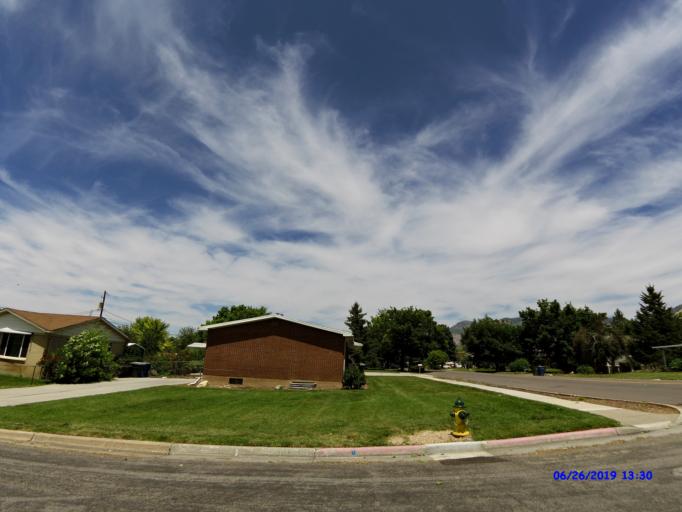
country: US
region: Utah
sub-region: Weber County
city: South Ogden
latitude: 41.2008
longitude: -111.9572
